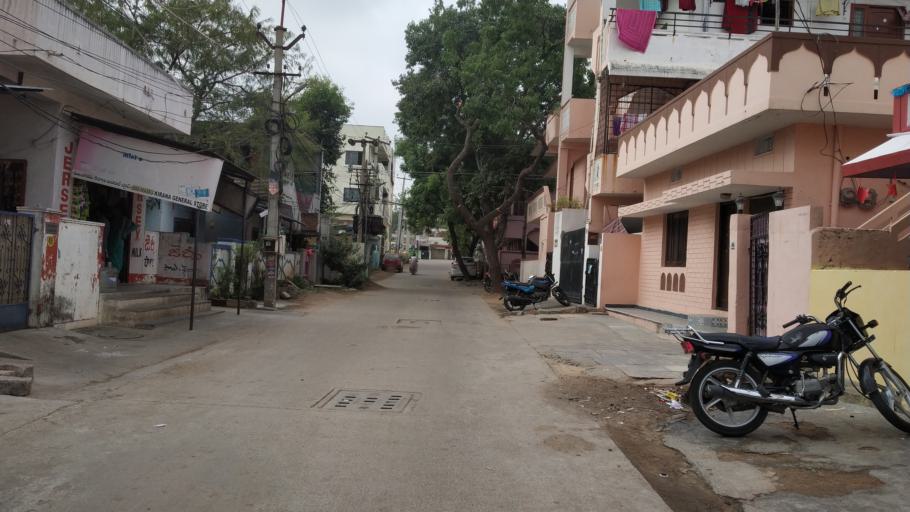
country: IN
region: Telangana
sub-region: Hyderabad
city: Malkajgiri
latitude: 17.4611
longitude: 78.5648
